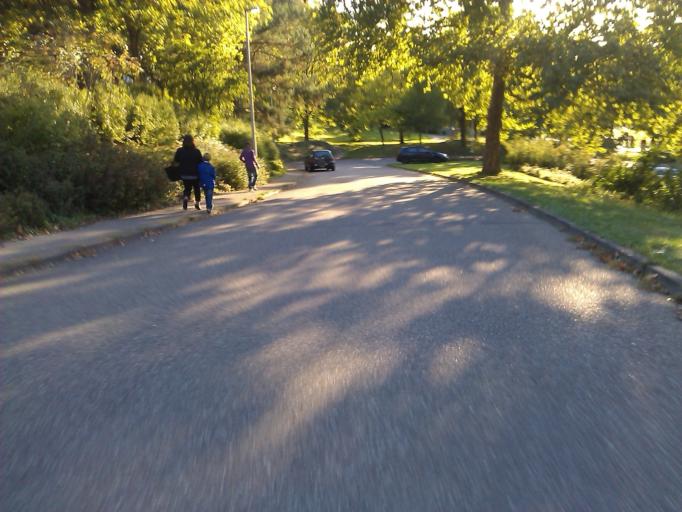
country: DE
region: Baden-Wuerttemberg
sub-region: Regierungsbezirk Stuttgart
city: Heilbronn
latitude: 49.1263
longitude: 9.2015
